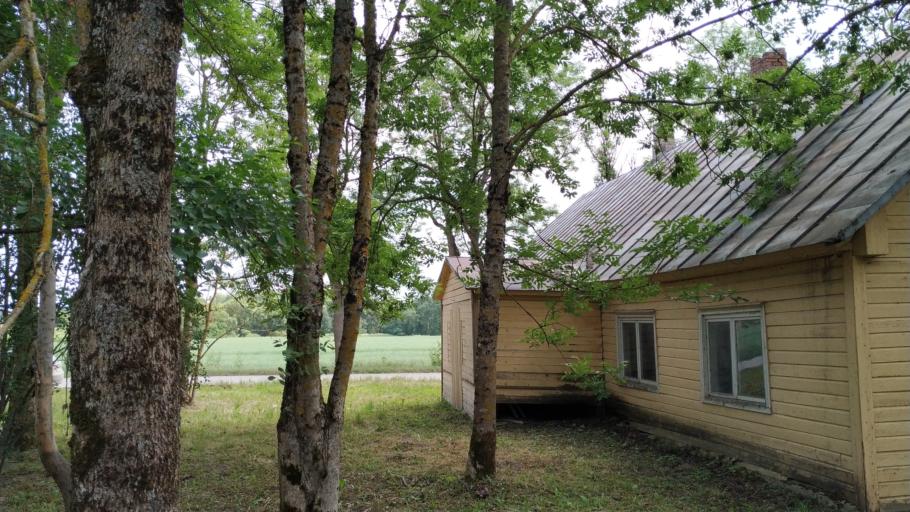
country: LT
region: Panevezys
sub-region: Birzai
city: Birzai
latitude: 56.3700
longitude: 24.7550
